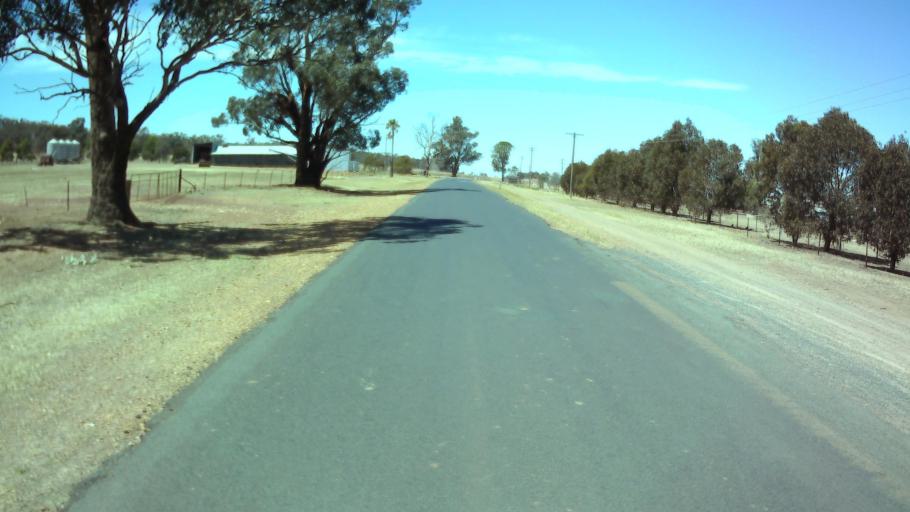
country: AU
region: New South Wales
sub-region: Weddin
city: Grenfell
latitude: -34.1011
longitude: 148.0068
